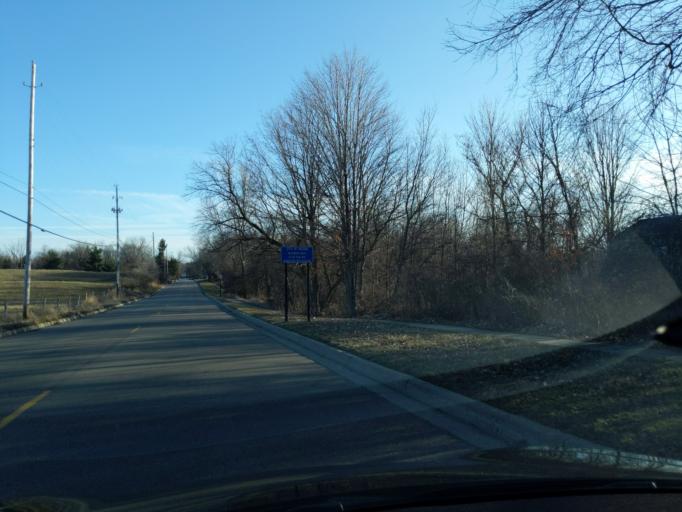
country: US
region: Michigan
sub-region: Ingham County
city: Mason
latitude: 42.5922
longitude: -84.4432
